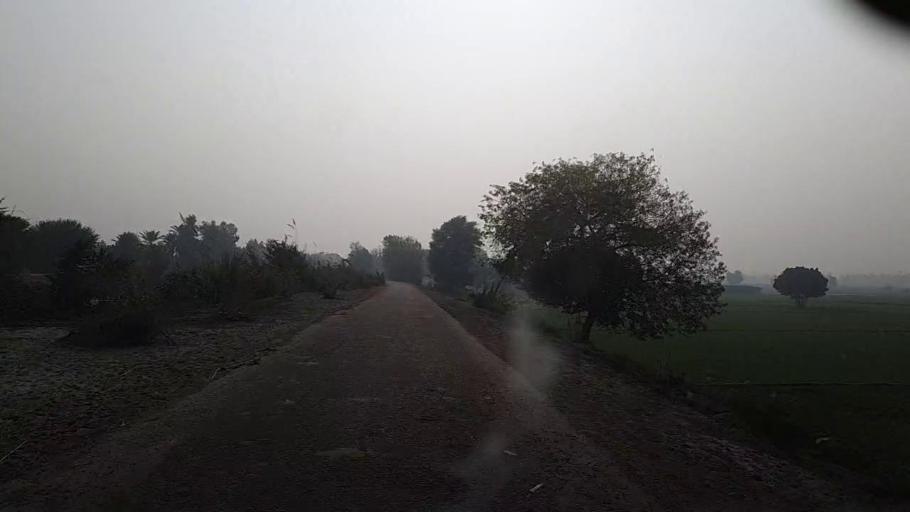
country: PK
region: Sindh
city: Bozdar
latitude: 27.1412
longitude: 68.6561
